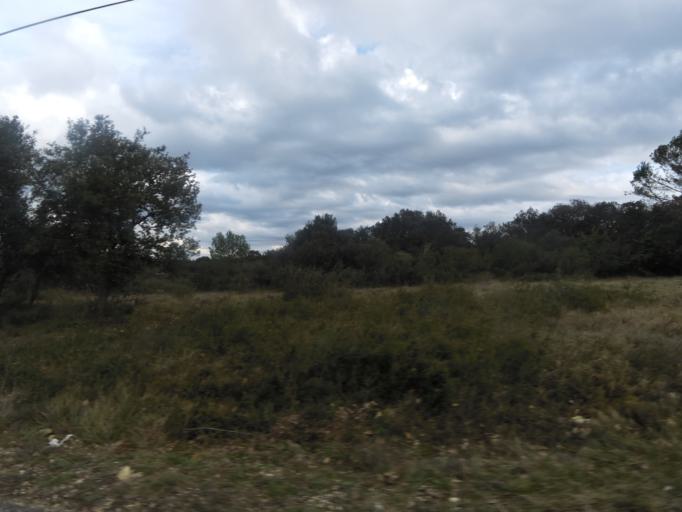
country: FR
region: Languedoc-Roussillon
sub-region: Departement du Gard
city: Saint-Mamert-du-Gard
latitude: 43.8544
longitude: 4.1888
